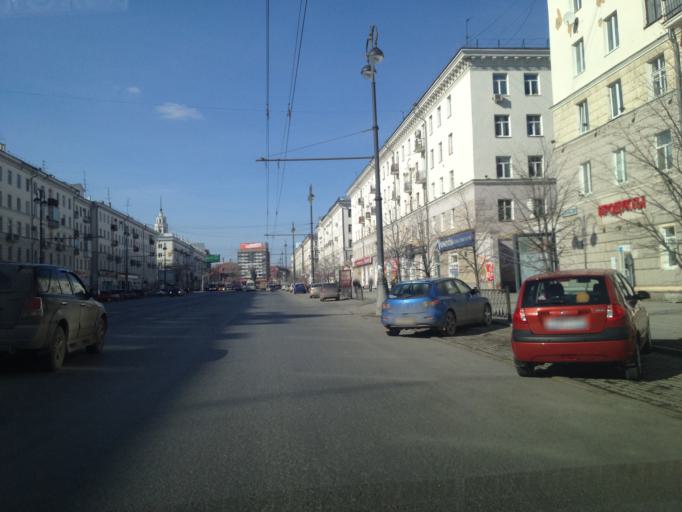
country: RU
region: Sverdlovsk
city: Yekaterinburg
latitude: 56.8518
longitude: 60.6054
